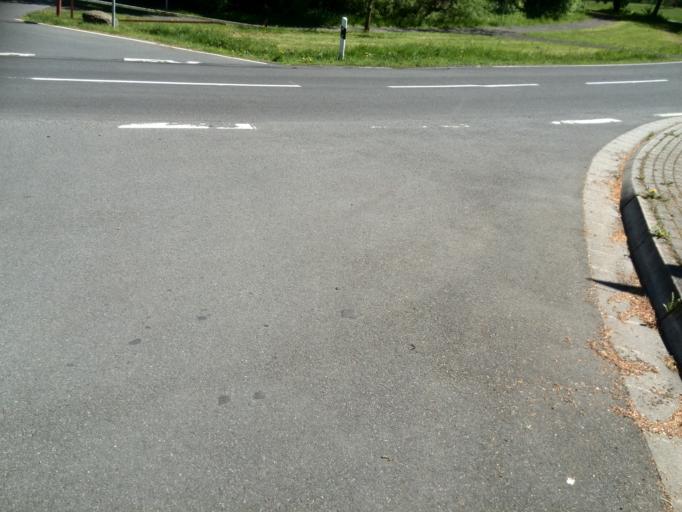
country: DE
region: Rheinland-Pfalz
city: Pottum
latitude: 50.5824
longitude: 7.9909
